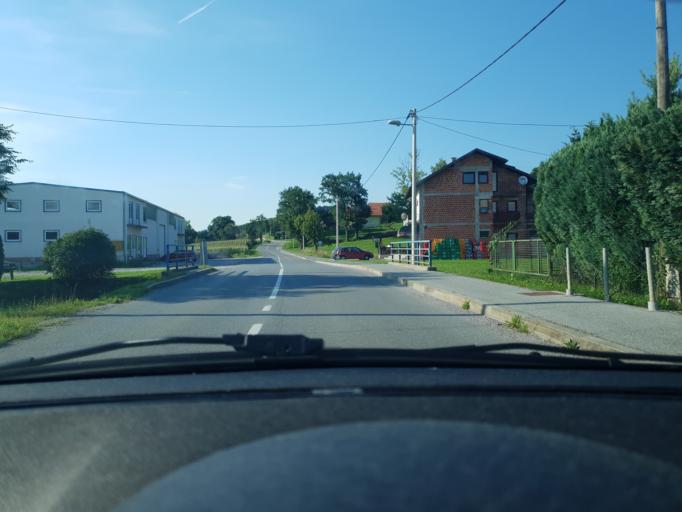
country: HR
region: Krapinsko-Zagorska
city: Zabok
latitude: 46.0690
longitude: 15.9238
